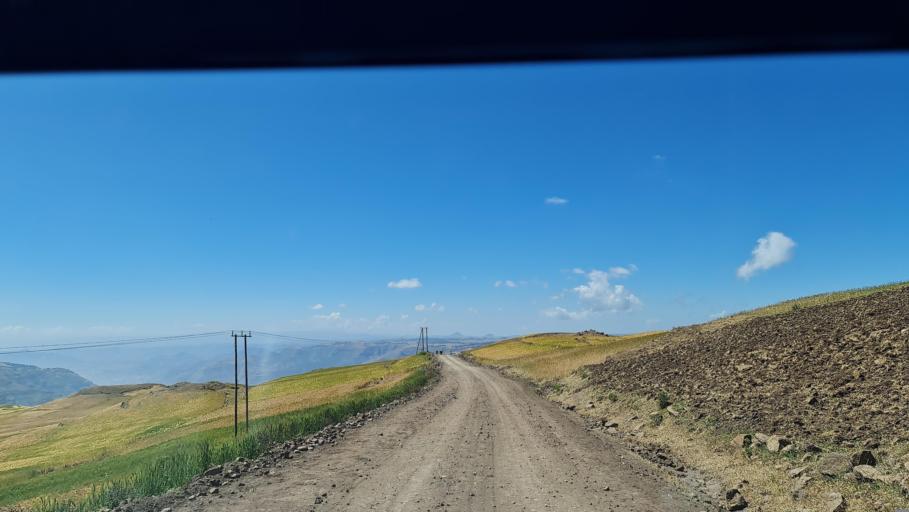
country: ET
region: Amhara
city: Debark'
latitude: 13.2352
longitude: 38.1077
